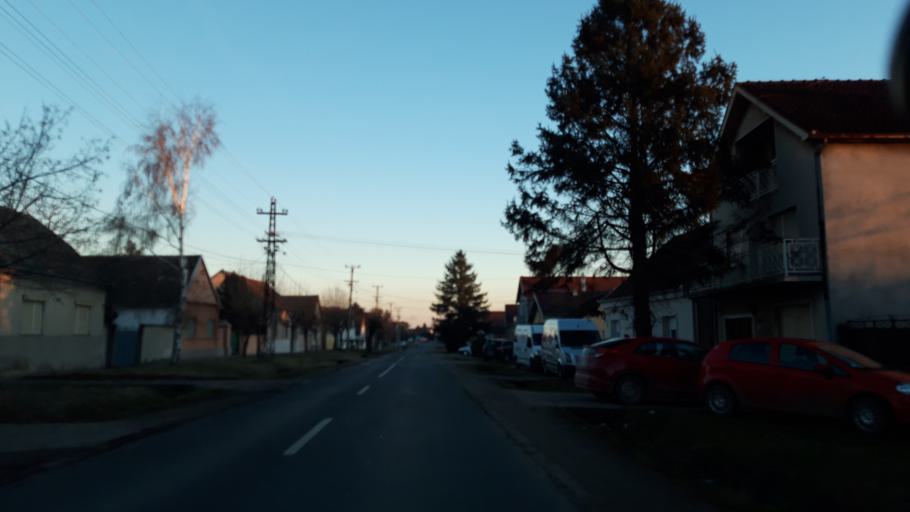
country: RS
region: Autonomna Pokrajina Vojvodina
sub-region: Sremski Okrug
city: Ingija
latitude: 45.0459
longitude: 20.0726
